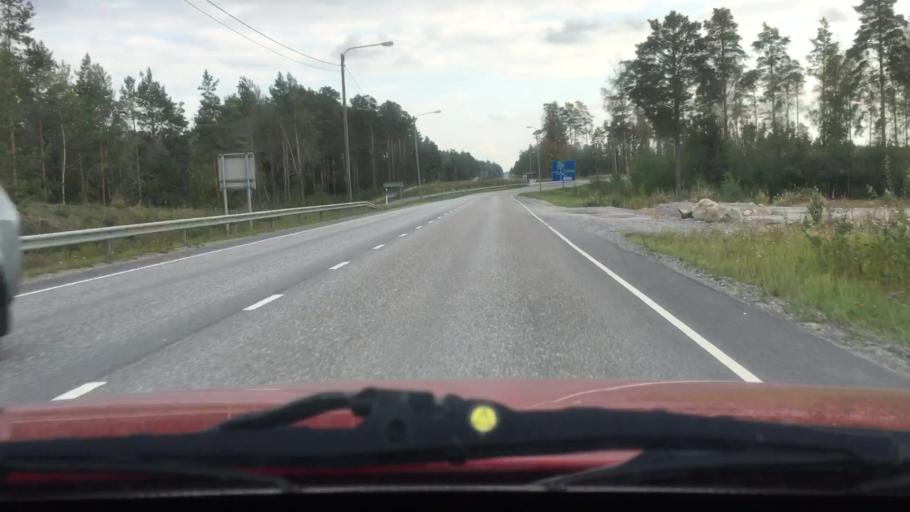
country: FI
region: Varsinais-Suomi
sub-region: Turku
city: Masku
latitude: 60.5449
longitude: 22.1283
